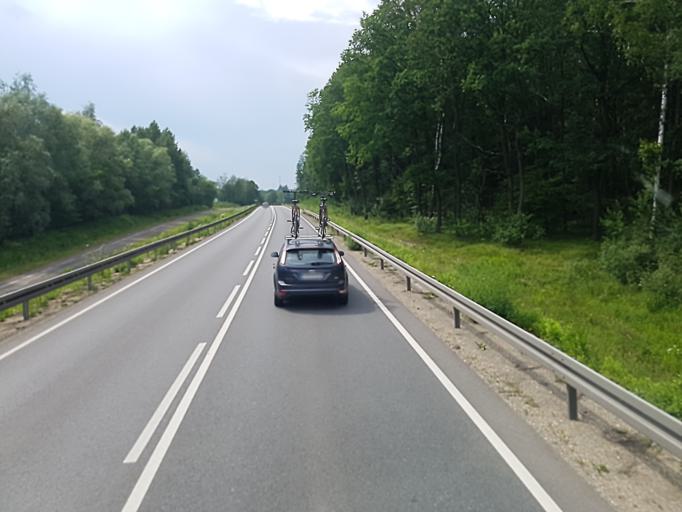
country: PL
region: Silesian Voivodeship
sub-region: Powiat pszczynski
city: Pawlowice
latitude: 49.9549
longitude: 18.6903
